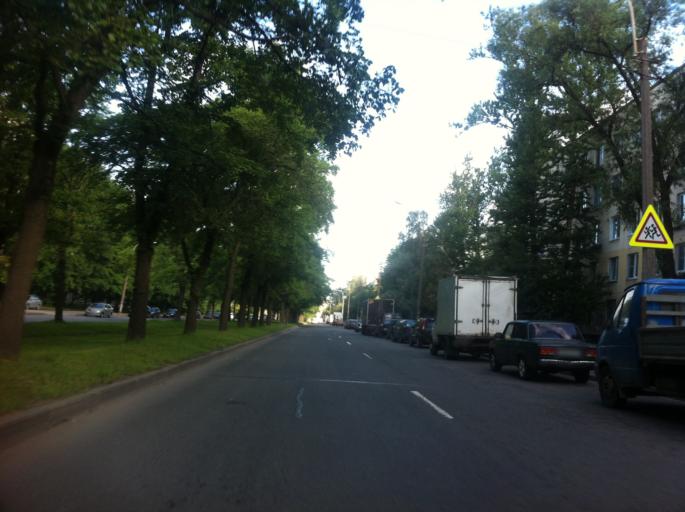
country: RU
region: St.-Petersburg
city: Dachnoye
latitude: 59.8411
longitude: 30.2708
